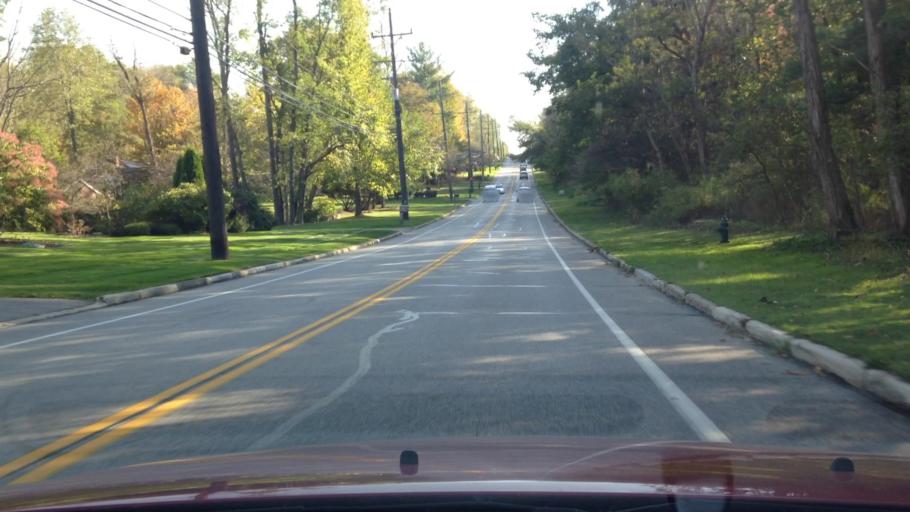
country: US
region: Ohio
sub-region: Cuyahoga County
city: Pepper Pike
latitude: 41.4769
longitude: -81.4634
